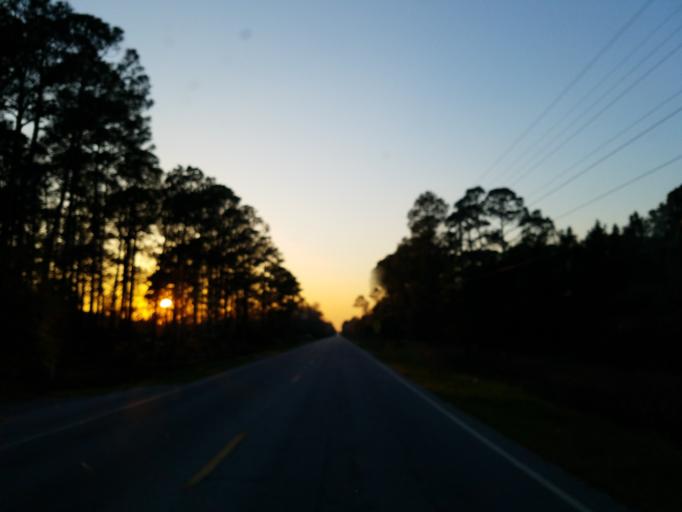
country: US
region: Georgia
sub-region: Lanier County
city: Lakeland
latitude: 31.0447
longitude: -83.1050
